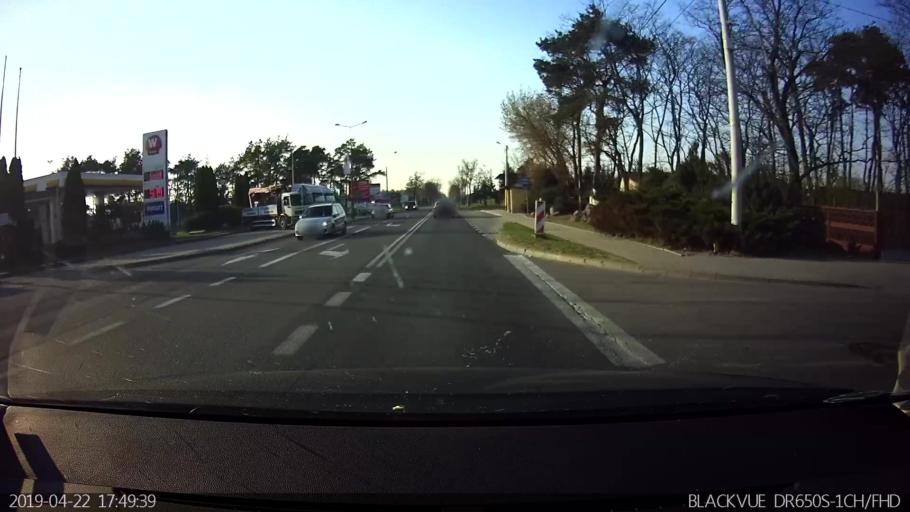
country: PL
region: Masovian Voivodeship
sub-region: Powiat wegrowski
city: Wegrow
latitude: 52.4160
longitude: 22.0075
